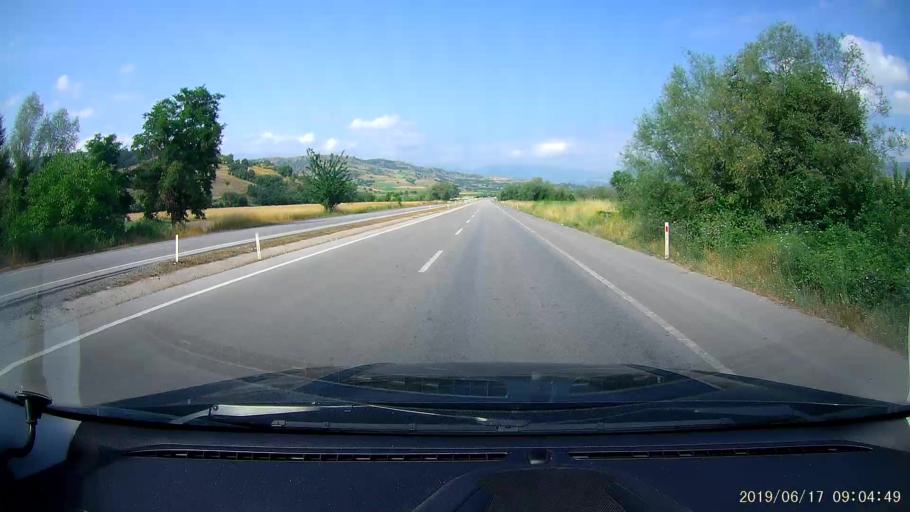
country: TR
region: Amasya
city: Tasova
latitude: 40.7420
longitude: 36.2798
